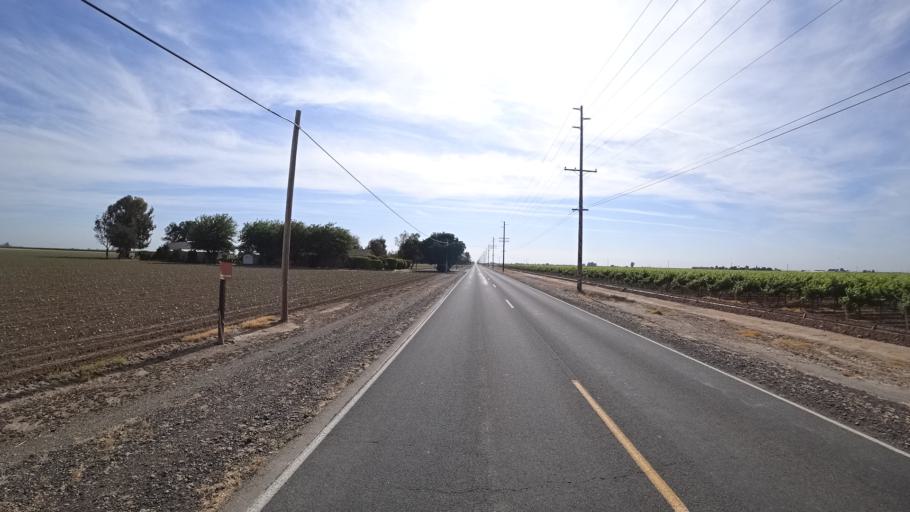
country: US
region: California
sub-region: Kings County
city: Hanford
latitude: 36.3427
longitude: -119.5780
